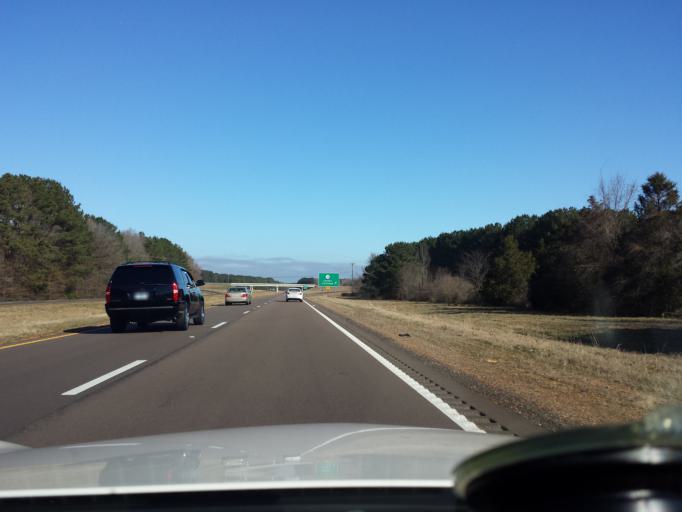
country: US
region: Mississippi
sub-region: Leake County
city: Carthage
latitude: 32.6969
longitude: -89.6314
